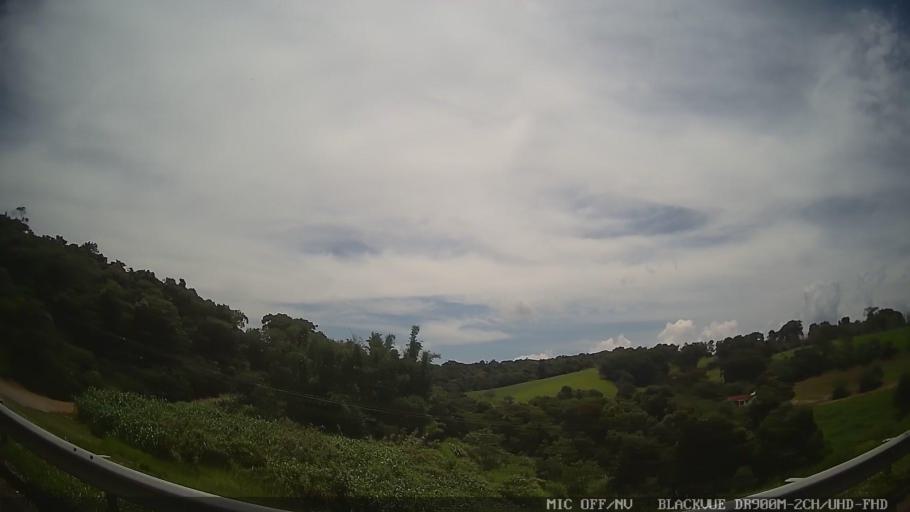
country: BR
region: Sao Paulo
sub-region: Jarinu
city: Jarinu
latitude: -23.0716
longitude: -46.6406
